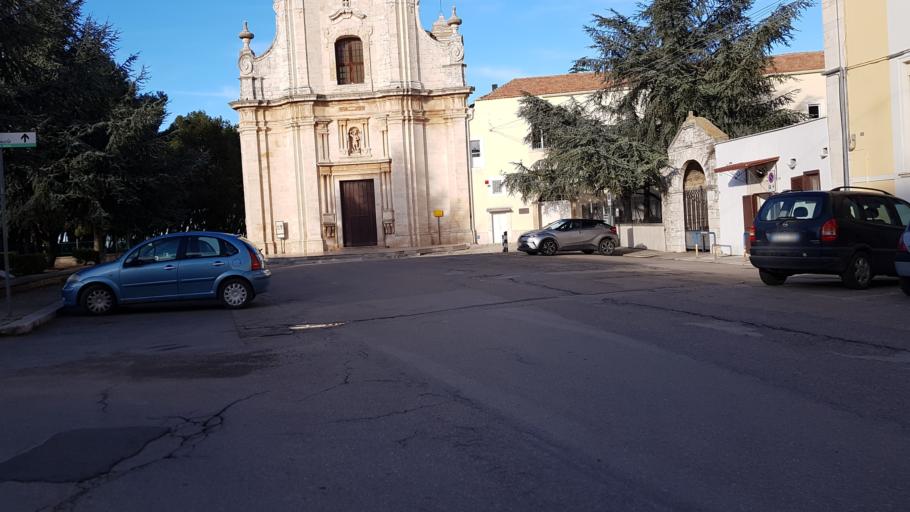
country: IT
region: Apulia
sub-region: Provincia di Bari
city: Ruvo di Puglia
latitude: 41.1206
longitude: 16.4873
